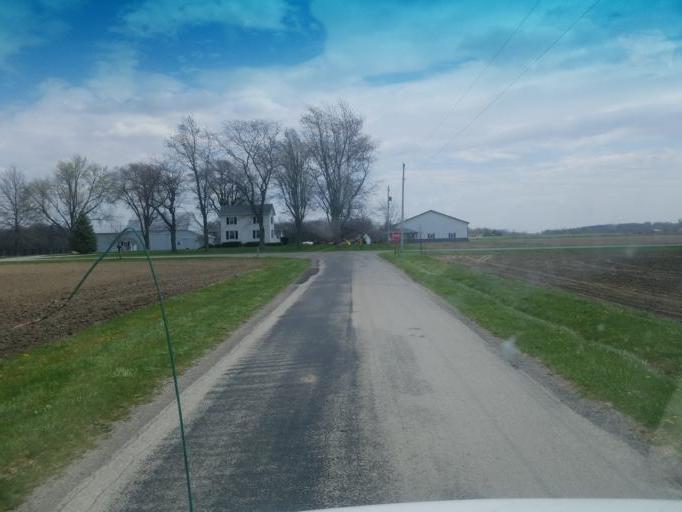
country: US
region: Ohio
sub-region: Wyandot County
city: Upper Sandusky
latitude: 40.7742
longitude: -83.3244
